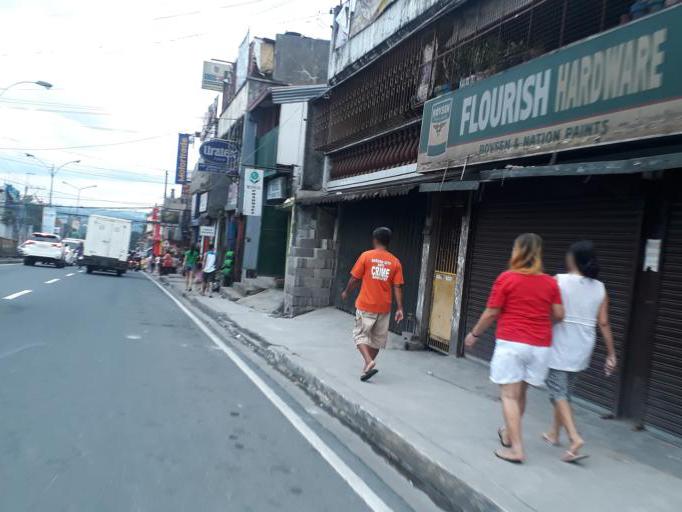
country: PH
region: Calabarzon
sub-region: Province of Rizal
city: San Mateo
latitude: 14.6898
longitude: 121.0974
